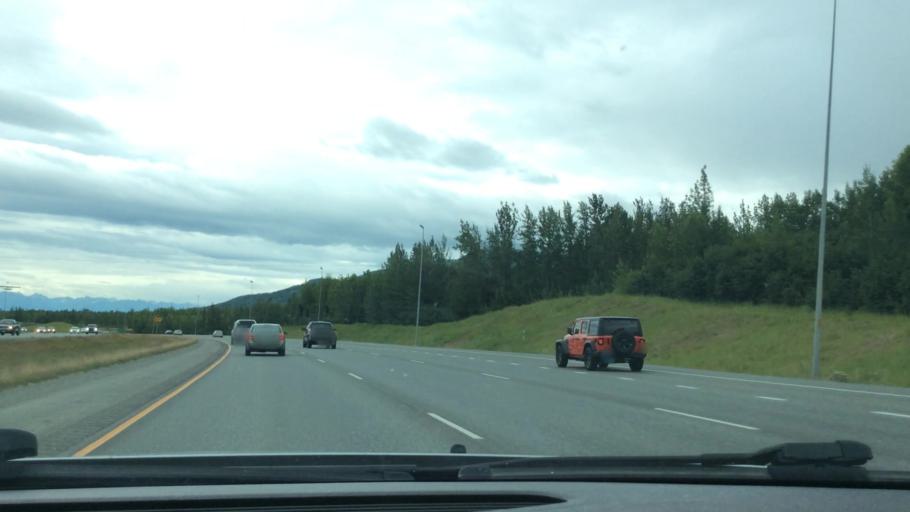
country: US
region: Alaska
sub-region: Anchorage Municipality
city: Eagle River
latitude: 61.2893
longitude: -149.5931
